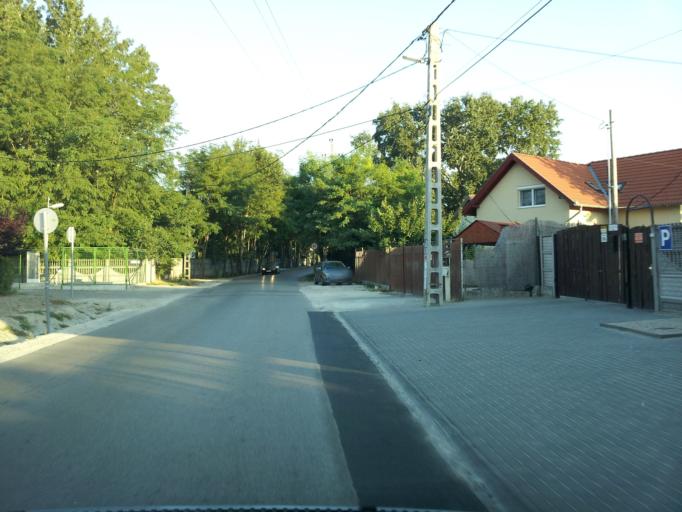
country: HU
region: Pest
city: Szigetszentmiklos
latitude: 47.3183
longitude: 19.0332
